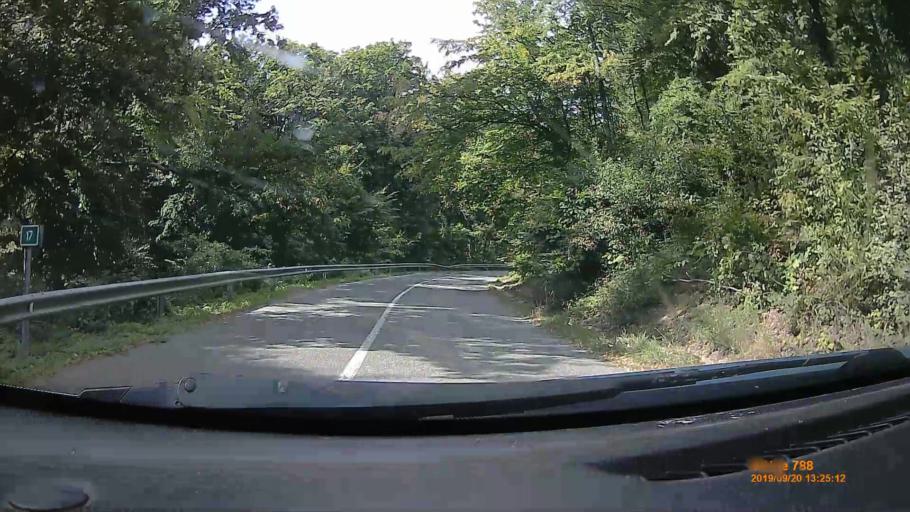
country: HU
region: Heves
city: Felsotarkany
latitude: 48.0422
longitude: 20.4867
